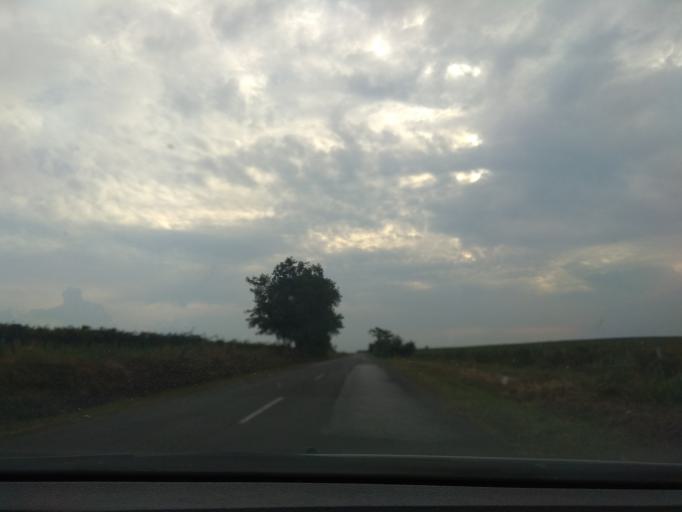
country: HU
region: Heves
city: Egerszalok
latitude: 47.8835
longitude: 20.3406
